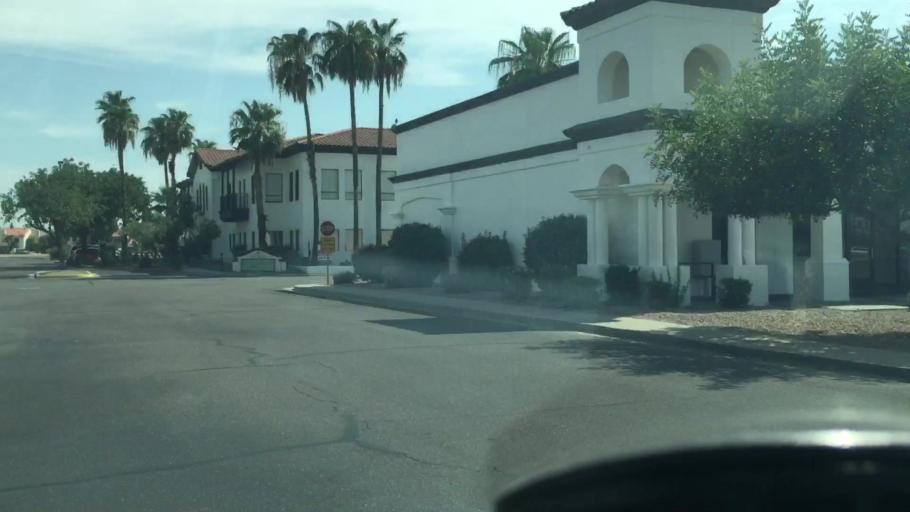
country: US
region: Arizona
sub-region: Maricopa County
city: Gilbert
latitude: 33.3779
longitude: -111.7526
